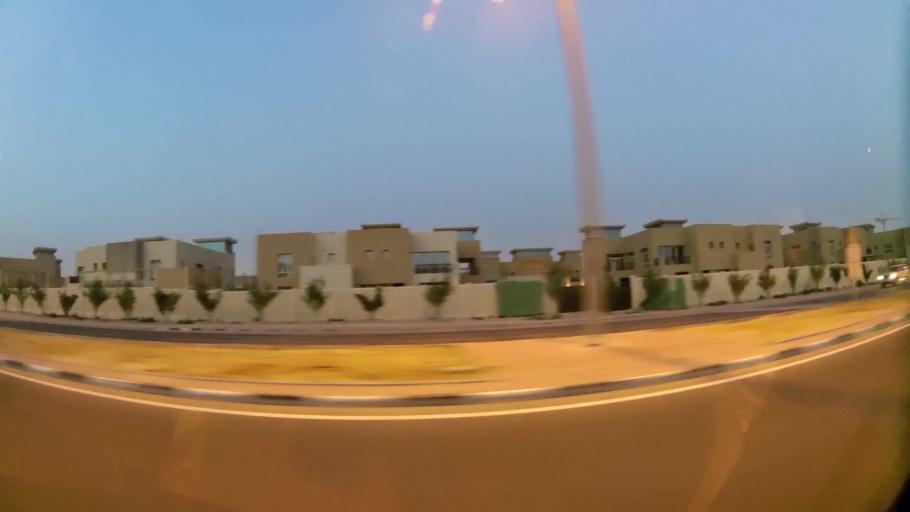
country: QA
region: Baladiyat ar Rayyan
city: Ar Rayyan
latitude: 25.2587
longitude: 51.4670
